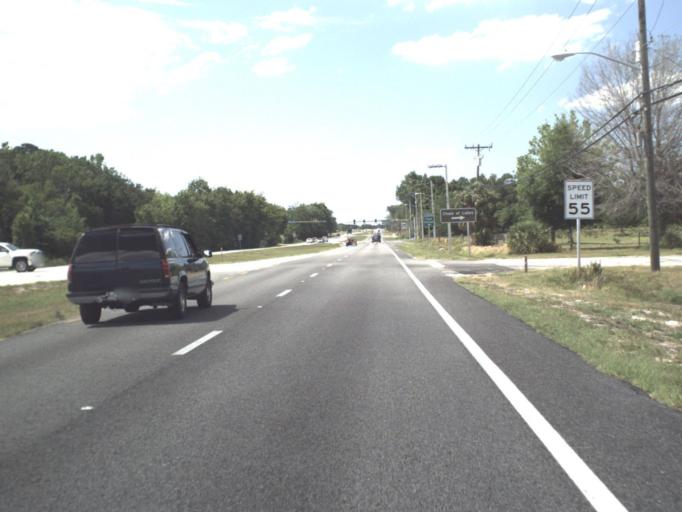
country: US
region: Florida
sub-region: Brevard County
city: Mims
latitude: 28.6379
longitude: -80.8302
